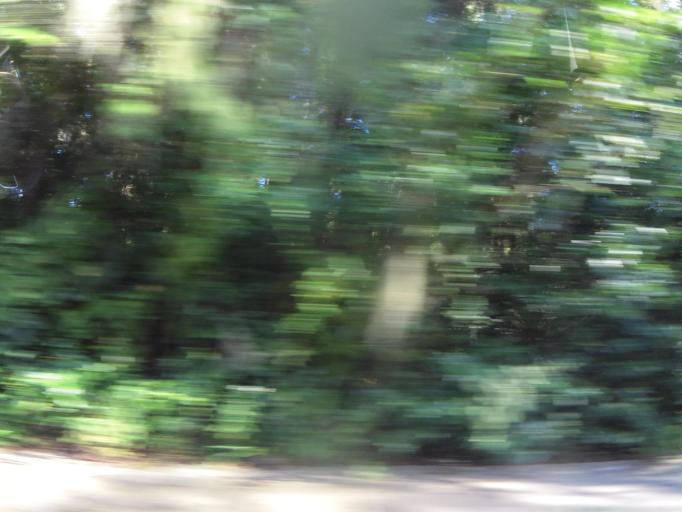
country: US
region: Florida
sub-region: Putnam County
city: Palatka
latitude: 29.6388
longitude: -81.6398
